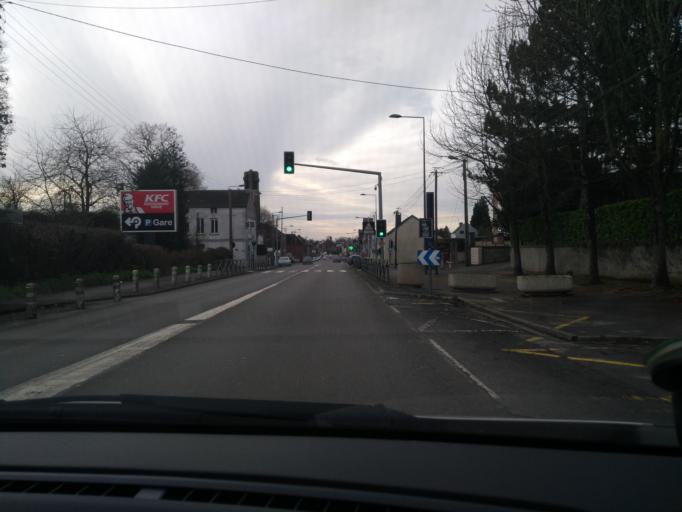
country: FR
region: Nord-Pas-de-Calais
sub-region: Departement du Nord
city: Maubeuge
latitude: 50.2922
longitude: 3.9755
